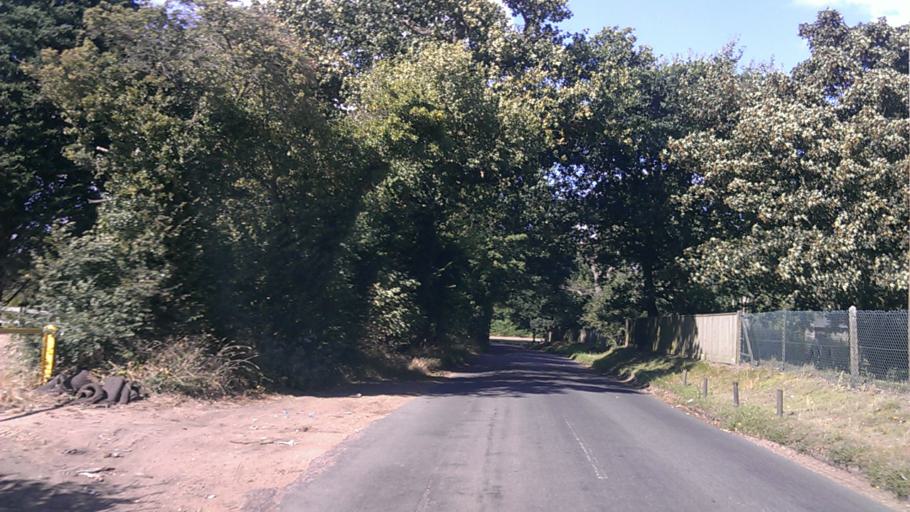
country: GB
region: England
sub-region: Essex
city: Layer de la Haye
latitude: 51.8591
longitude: 0.8833
